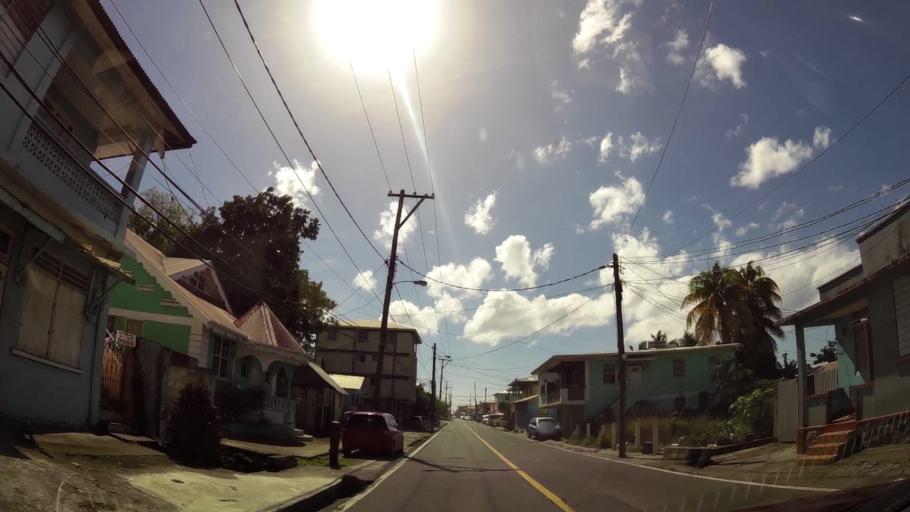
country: DM
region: Saint George
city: Roseau
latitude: 15.3039
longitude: -61.3900
